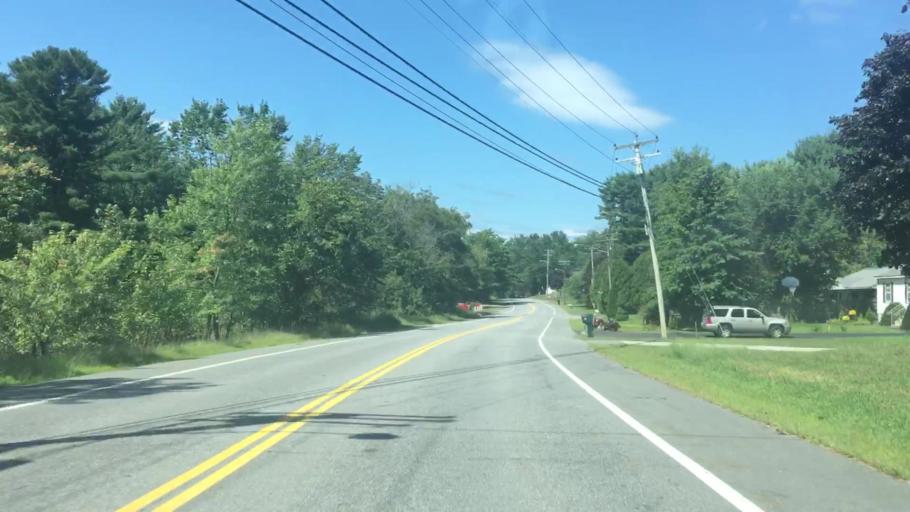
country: US
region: Maine
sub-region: Androscoggin County
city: Sabattus
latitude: 44.0904
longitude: -70.1469
